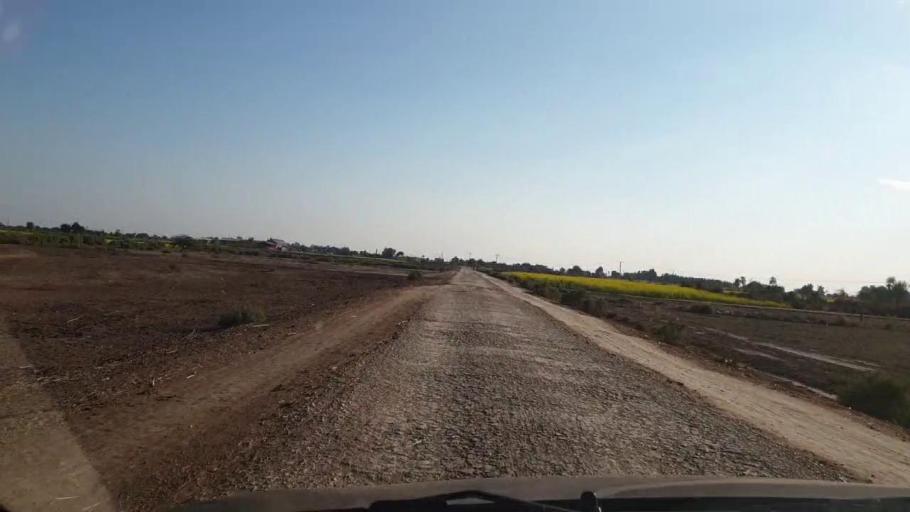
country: PK
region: Sindh
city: Jhol
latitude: 25.9574
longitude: 68.8615
